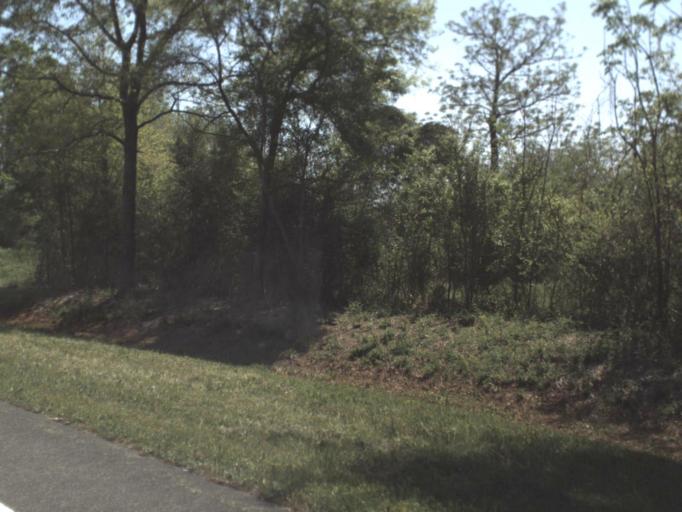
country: US
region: Alabama
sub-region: Escambia County
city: East Brewton
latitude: 30.9294
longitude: -87.0559
